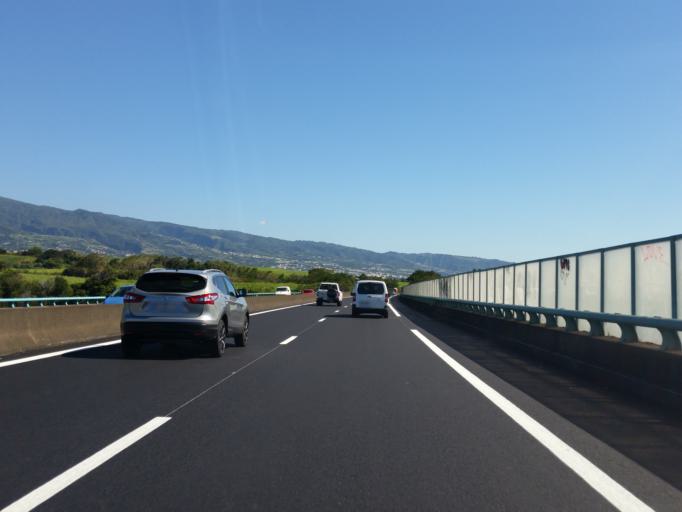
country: RE
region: Reunion
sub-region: Reunion
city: Sainte-Marie
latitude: -20.9025
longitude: 55.5560
